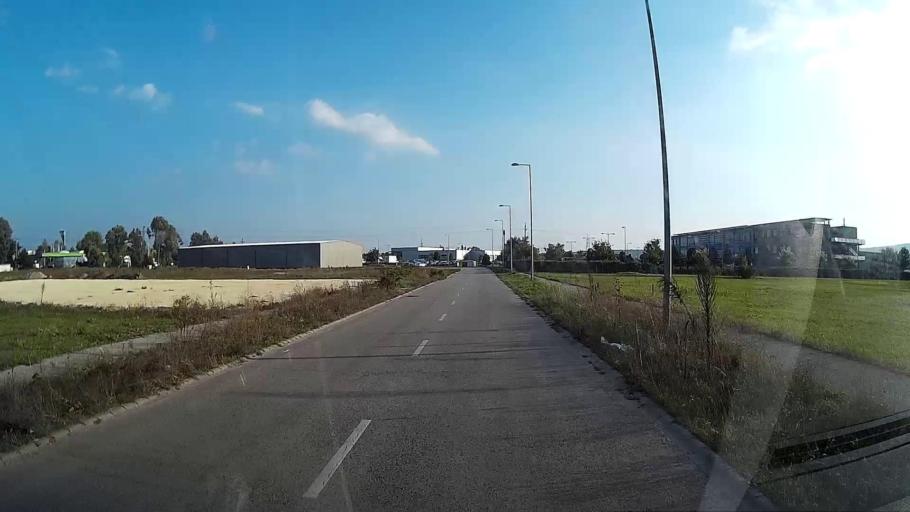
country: HU
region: Pest
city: Szentendre
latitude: 47.6429
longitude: 19.0655
